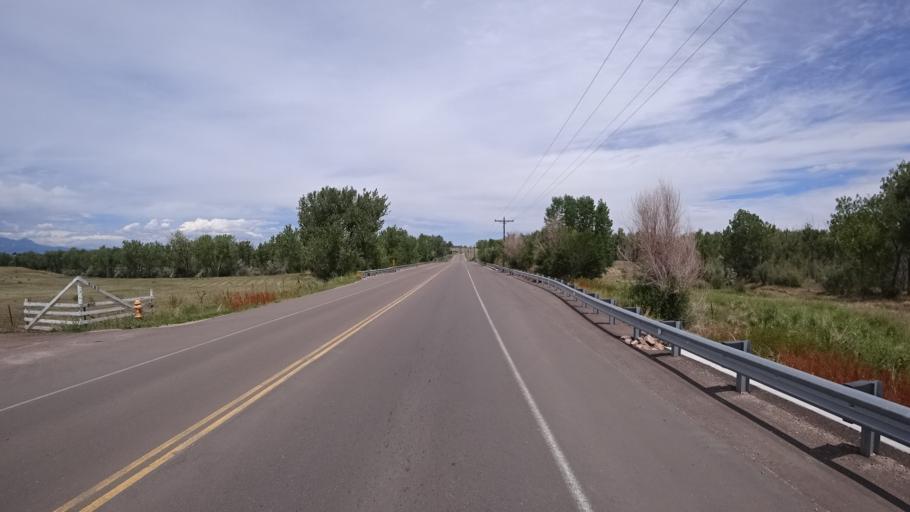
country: US
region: Colorado
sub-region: El Paso County
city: Fountain
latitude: 38.7000
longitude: -104.6737
